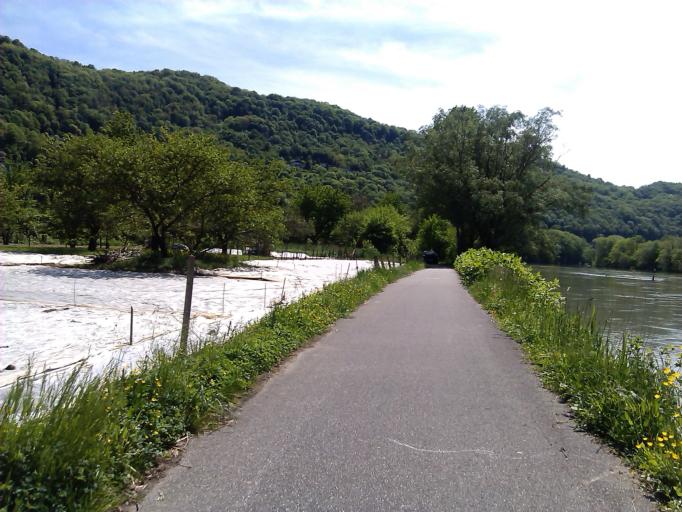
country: FR
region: Franche-Comte
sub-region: Departement du Doubs
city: Beure
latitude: 47.2073
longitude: 5.9953
